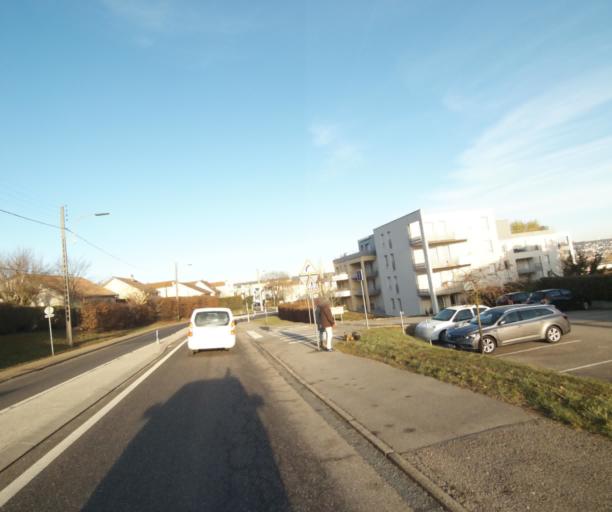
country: FR
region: Lorraine
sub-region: Departement de Meurthe-et-Moselle
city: Villers-les-Nancy
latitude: 48.6622
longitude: 6.1638
